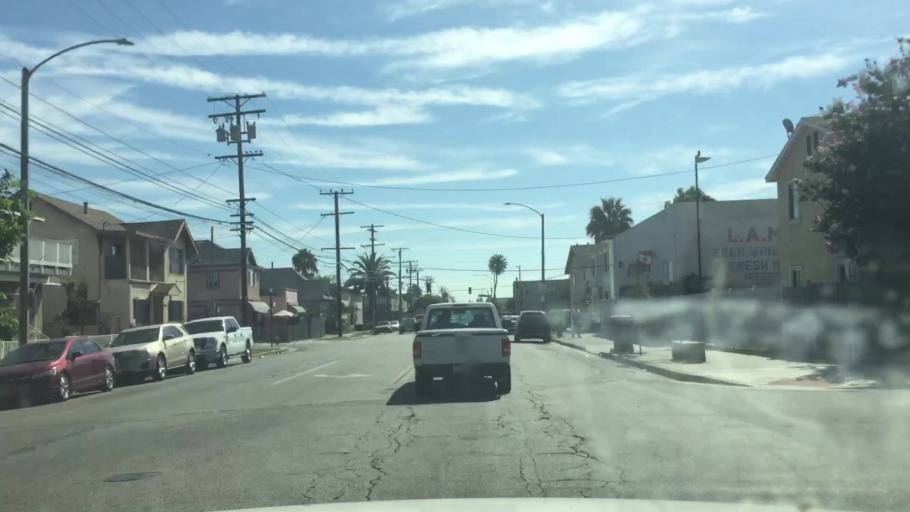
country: US
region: California
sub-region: Los Angeles County
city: Long Beach
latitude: 33.7789
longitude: -118.1824
